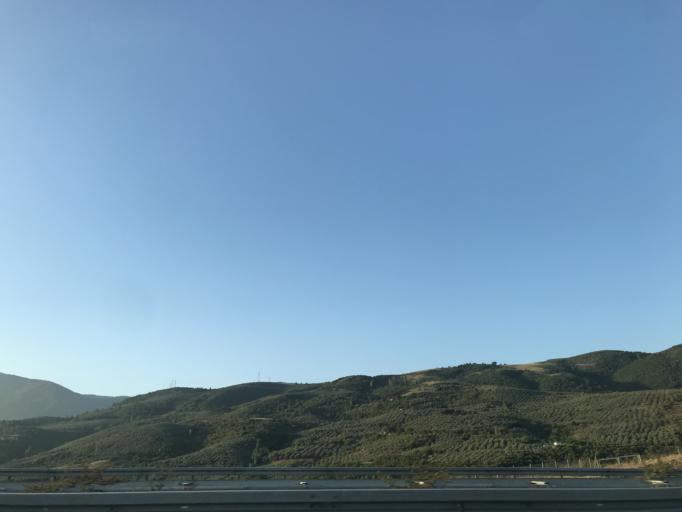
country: TR
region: Bursa
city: Umurbey
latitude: 40.4289
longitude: 29.2257
